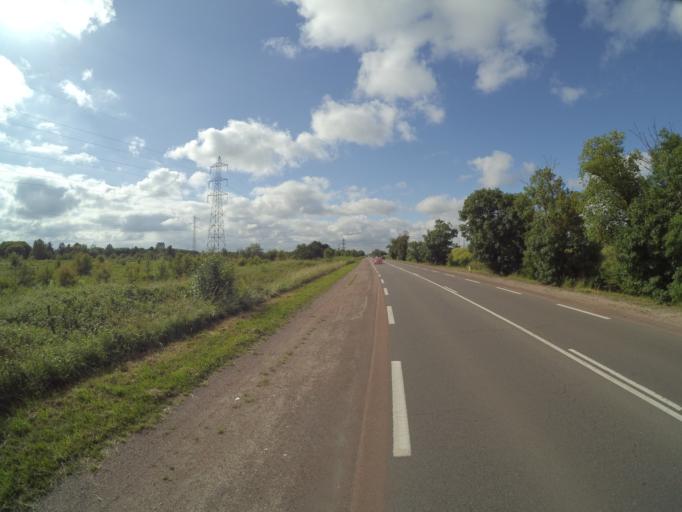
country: FR
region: Aquitaine
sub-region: Departement de la Gironde
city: Bassens
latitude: 44.9029
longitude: -0.5534
